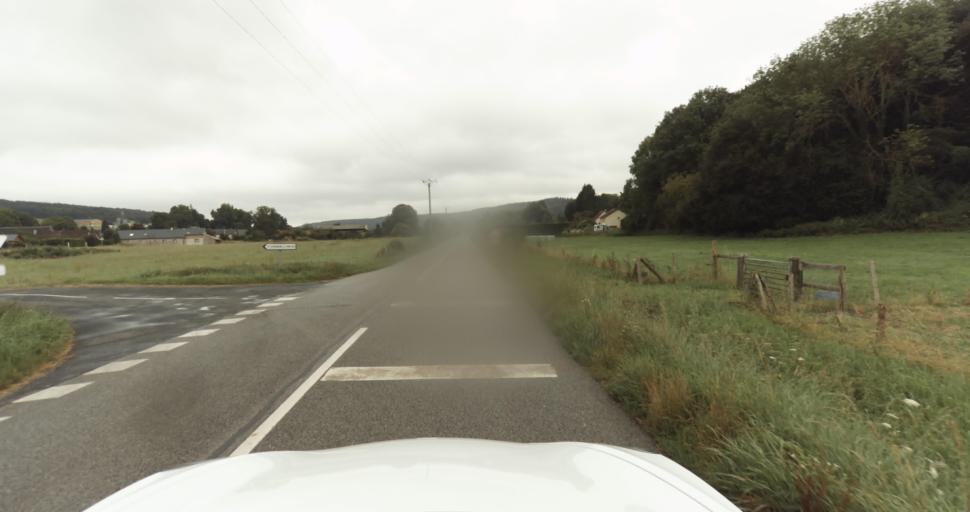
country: FR
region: Haute-Normandie
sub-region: Departement de l'Eure
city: Normanville
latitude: 49.0937
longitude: 1.1369
